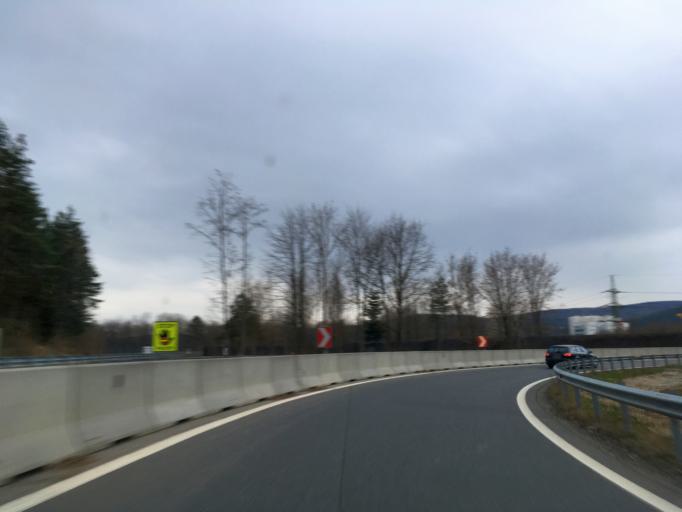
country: AT
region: Lower Austria
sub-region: Politischer Bezirk Wien-Umgebung
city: Pressbaum
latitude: 48.1741
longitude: 16.0590
